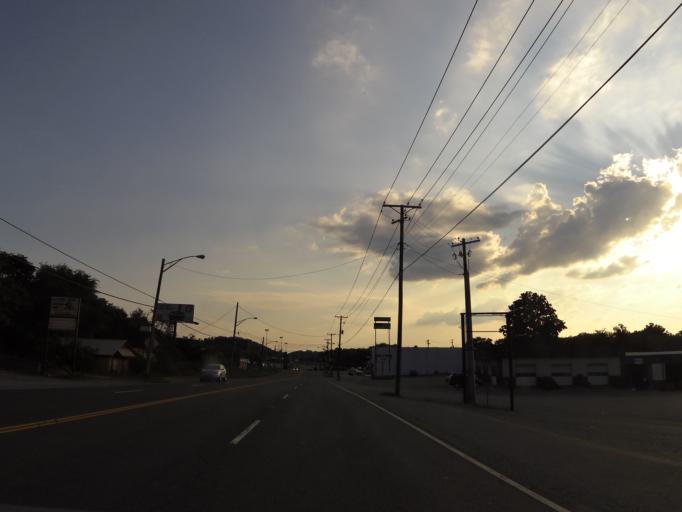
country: US
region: Tennessee
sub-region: Knox County
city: Knoxville
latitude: 36.0122
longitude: -83.8685
